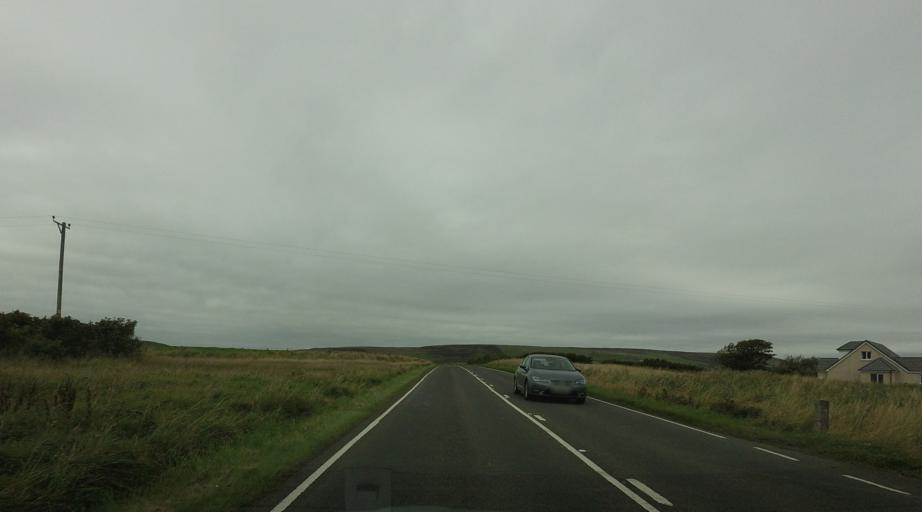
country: GB
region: Scotland
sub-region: Orkney Islands
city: Orkney
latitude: 58.9994
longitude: -3.0901
